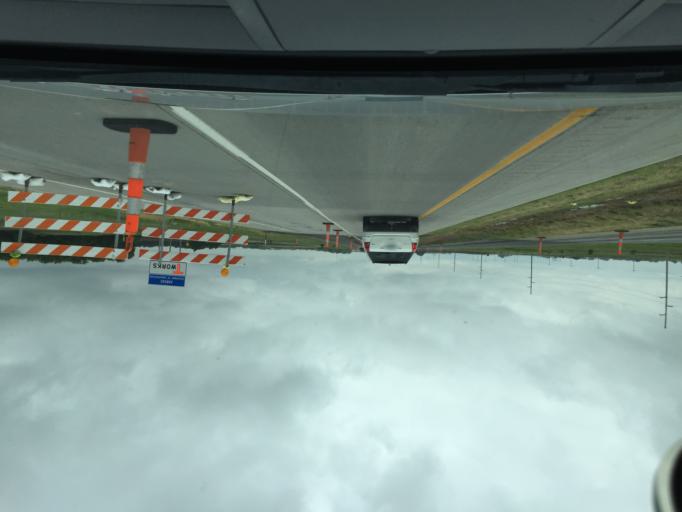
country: US
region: Kansas
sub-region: Reno County
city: South Hutchinson
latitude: 38.0133
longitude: -97.9465
